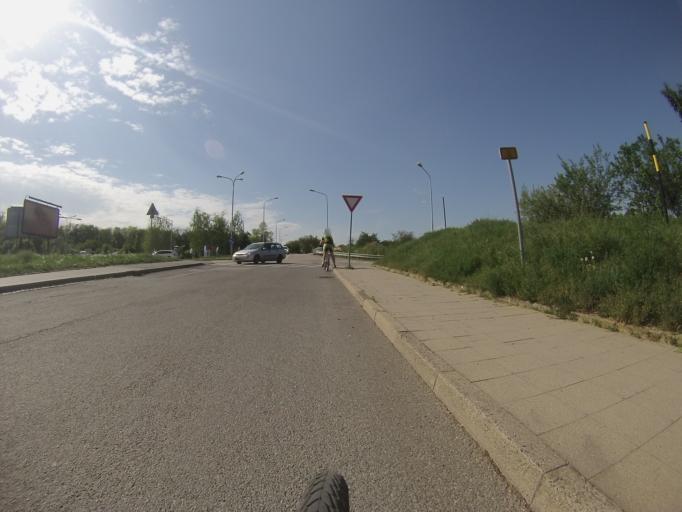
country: CZ
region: South Moravian
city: Troubsko
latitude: 49.2282
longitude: 16.5236
